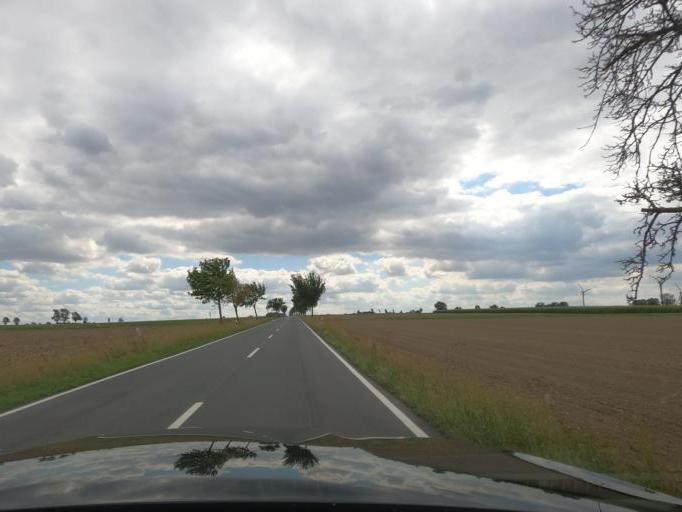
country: DE
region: Lower Saxony
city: Hohenhameln
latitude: 52.2967
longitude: 10.0450
